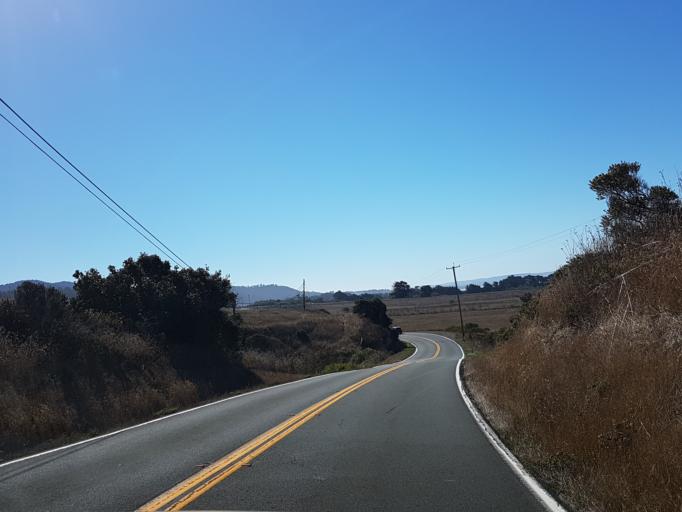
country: US
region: California
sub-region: Mendocino County
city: Boonville
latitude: 39.0762
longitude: -123.6943
